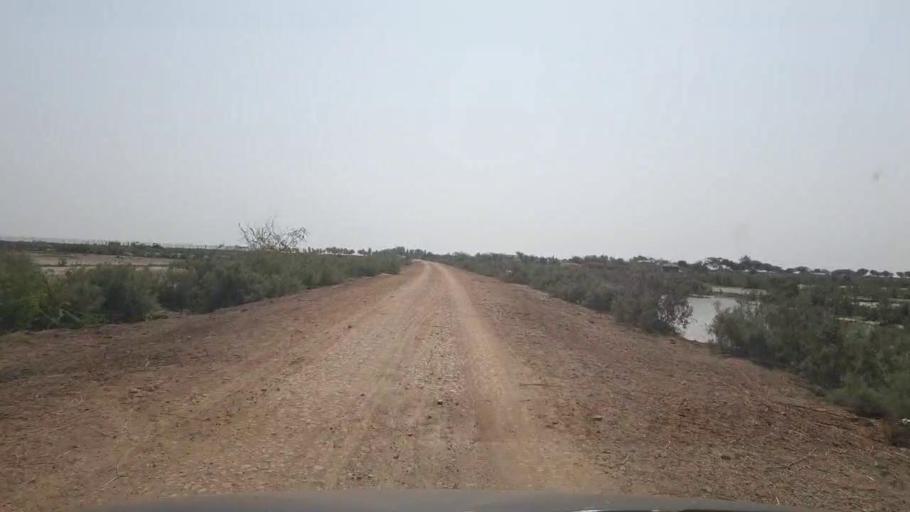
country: PK
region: Sindh
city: Jati
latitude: 24.3844
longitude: 68.5997
